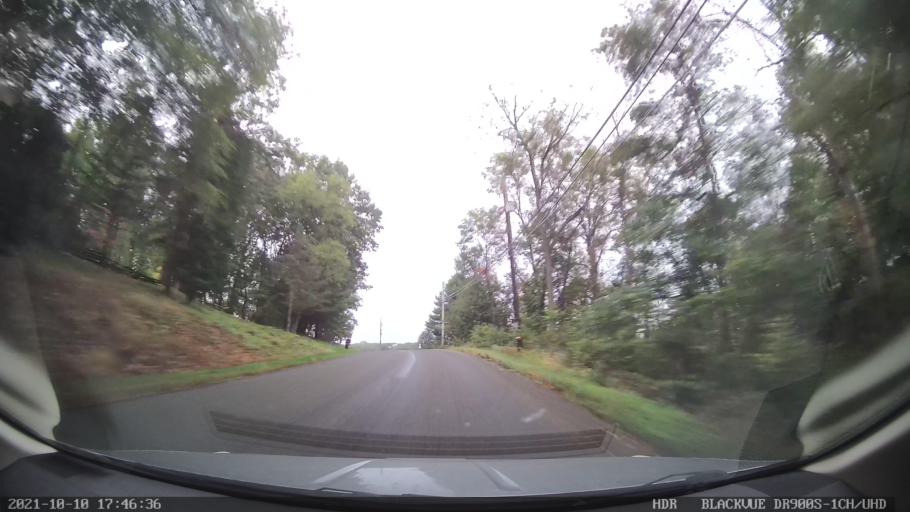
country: US
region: Pennsylvania
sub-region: Lehigh County
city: Breinigsville
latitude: 40.5661
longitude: -75.6745
